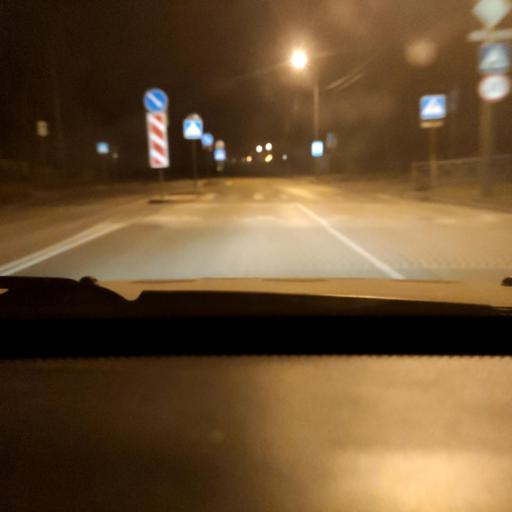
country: RU
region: Perm
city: Polazna
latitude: 58.1201
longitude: 56.4032
